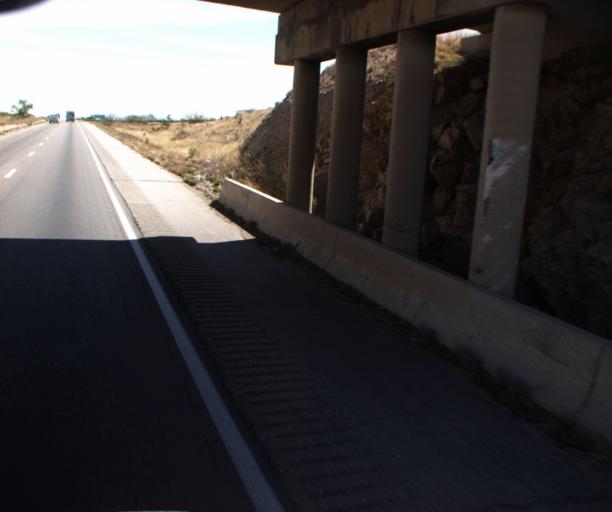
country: US
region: Arizona
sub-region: Cochise County
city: Saint David
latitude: 32.0816
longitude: -110.0517
